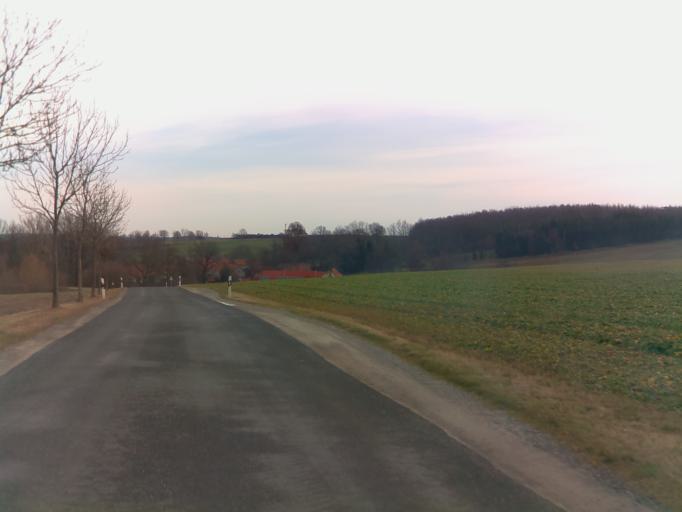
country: DE
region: Thuringia
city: Hundhaupten
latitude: 50.8251
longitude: 11.9814
